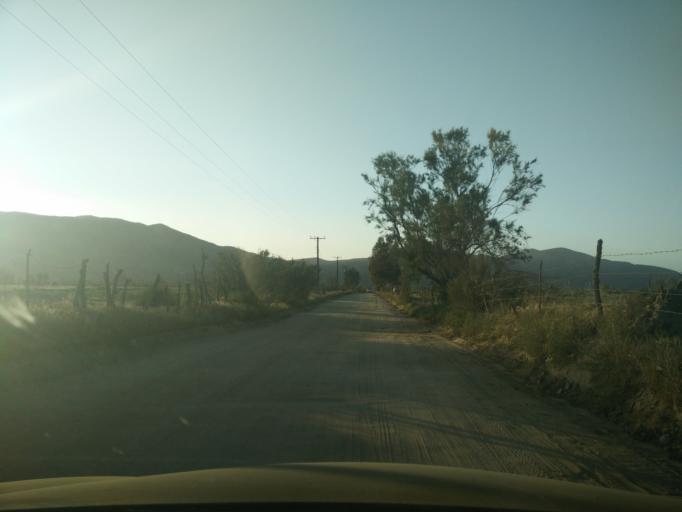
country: MX
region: Baja California
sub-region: Ensenada
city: Rancho Verde
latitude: 32.0518
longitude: -116.6433
